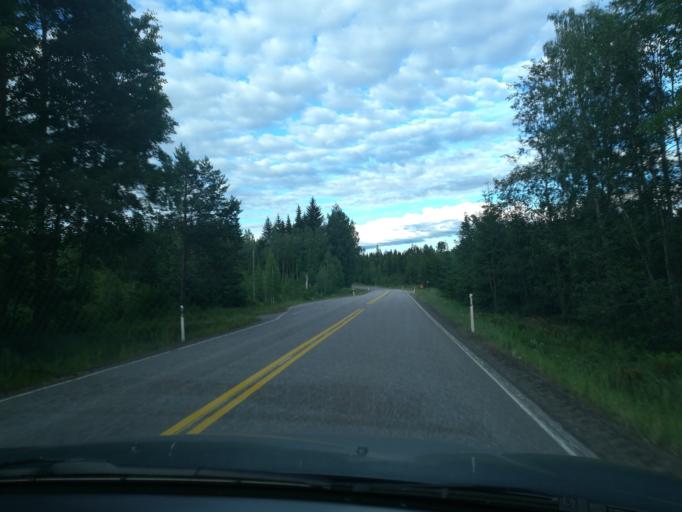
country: FI
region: Southern Savonia
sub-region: Mikkeli
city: Puumala
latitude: 61.5234
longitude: 27.9286
